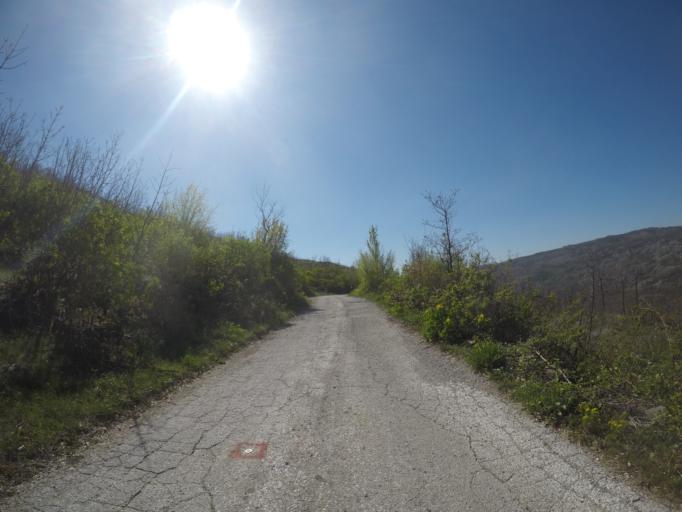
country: ME
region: Danilovgrad
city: Danilovgrad
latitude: 42.5354
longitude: 19.0159
